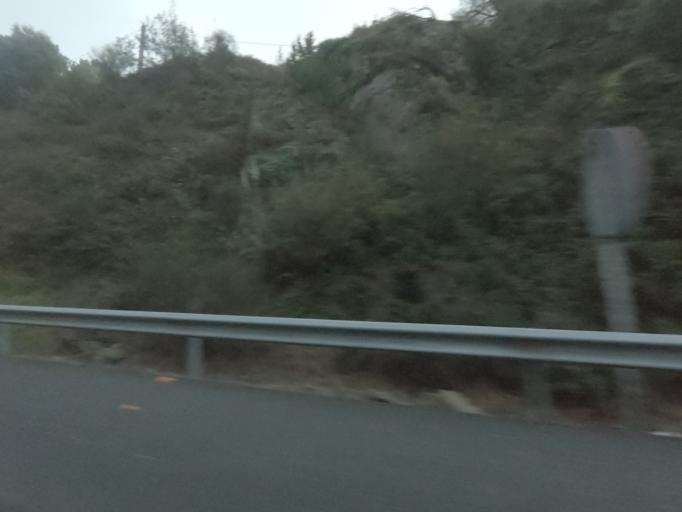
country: ES
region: Galicia
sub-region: Provincia de Pontevedra
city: Redondela
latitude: 42.3316
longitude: -8.6482
